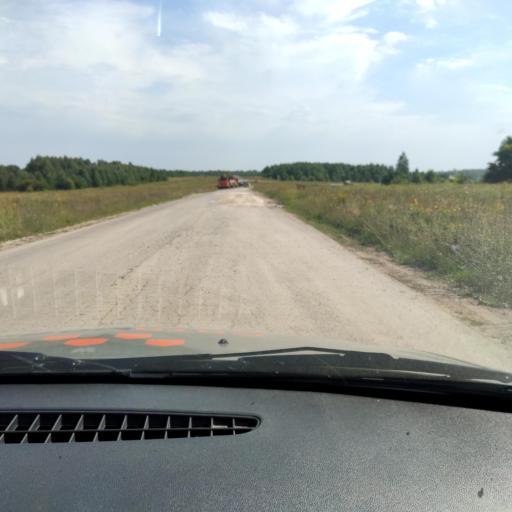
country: RU
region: Bashkortostan
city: Pavlovka
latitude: 55.3933
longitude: 56.4629
